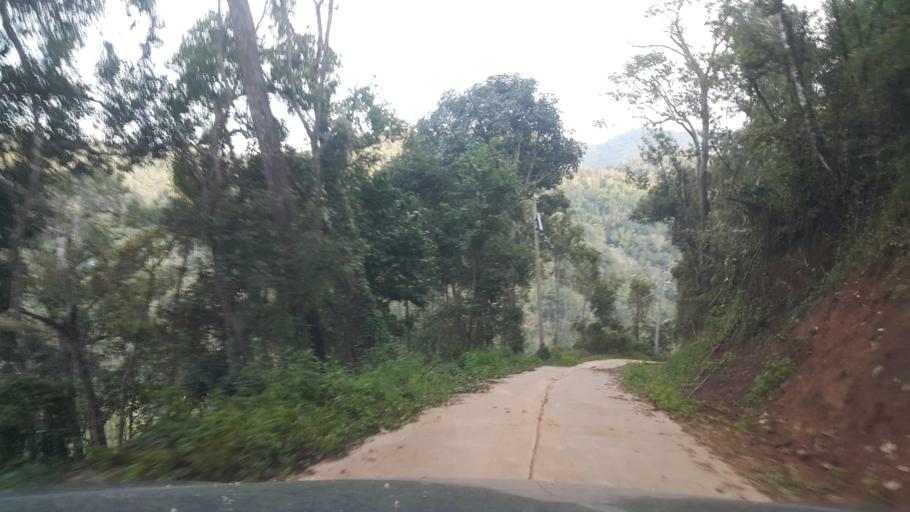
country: TH
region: Chiang Mai
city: Samoeng
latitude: 19.0092
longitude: 98.6687
